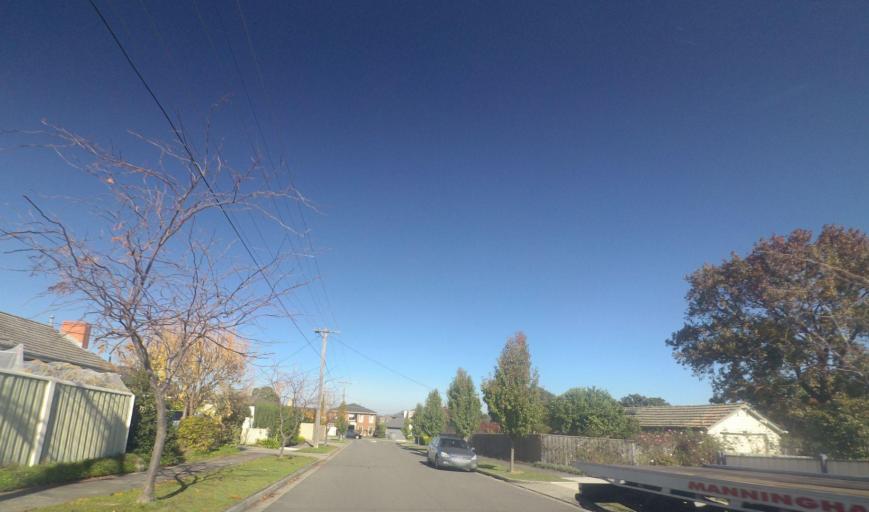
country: AU
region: Victoria
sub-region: Manningham
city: Doncaster East
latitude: -37.7928
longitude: 145.1379
